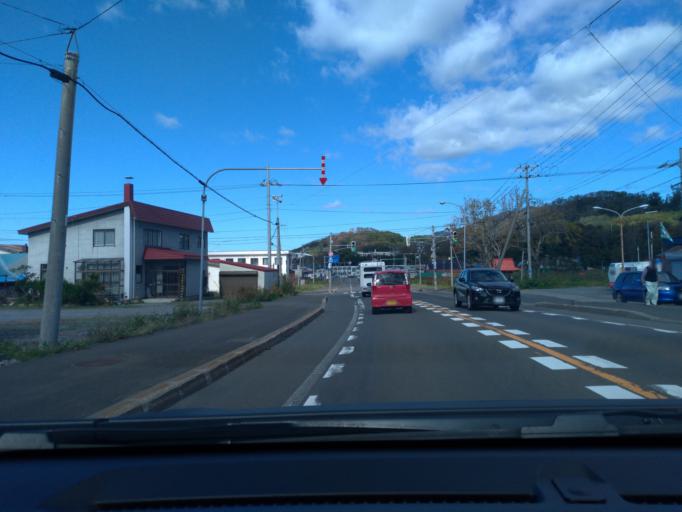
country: JP
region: Hokkaido
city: Ishikari
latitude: 43.3971
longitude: 141.4372
